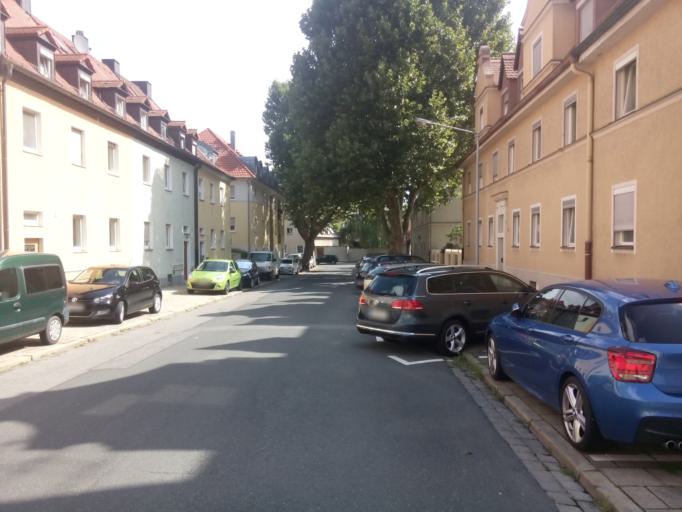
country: DE
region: Bavaria
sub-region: Upper Franconia
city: Bamberg
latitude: 49.8924
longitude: 10.9020
